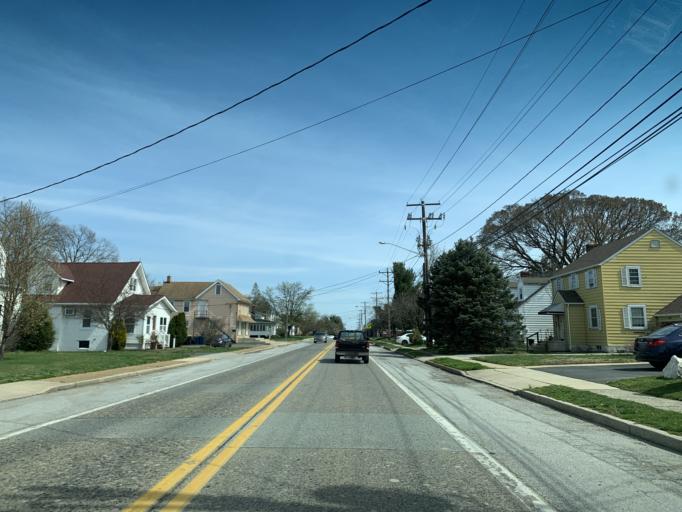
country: US
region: Delaware
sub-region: New Castle County
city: Newport
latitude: 39.7246
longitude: -75.6062
